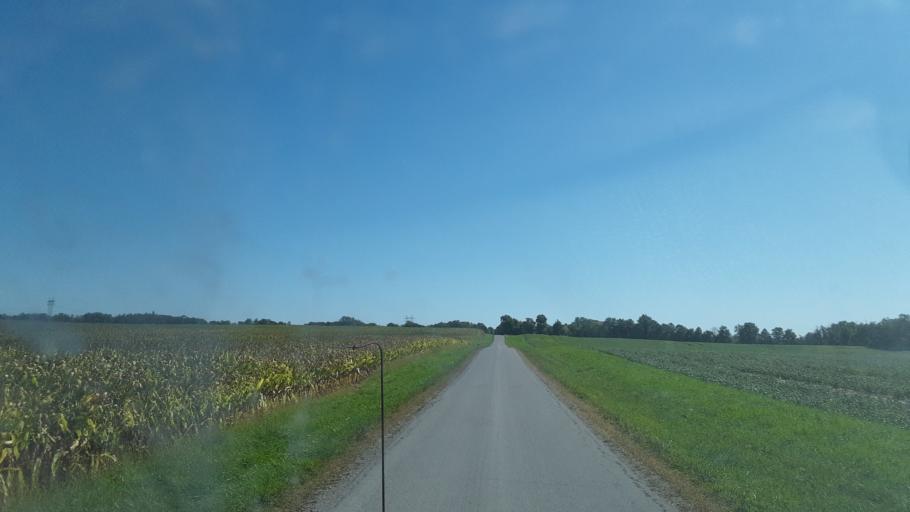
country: US
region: Ohio
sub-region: Wyandot County
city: Upper Sandusky
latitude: 40.9350
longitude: -83.2062
